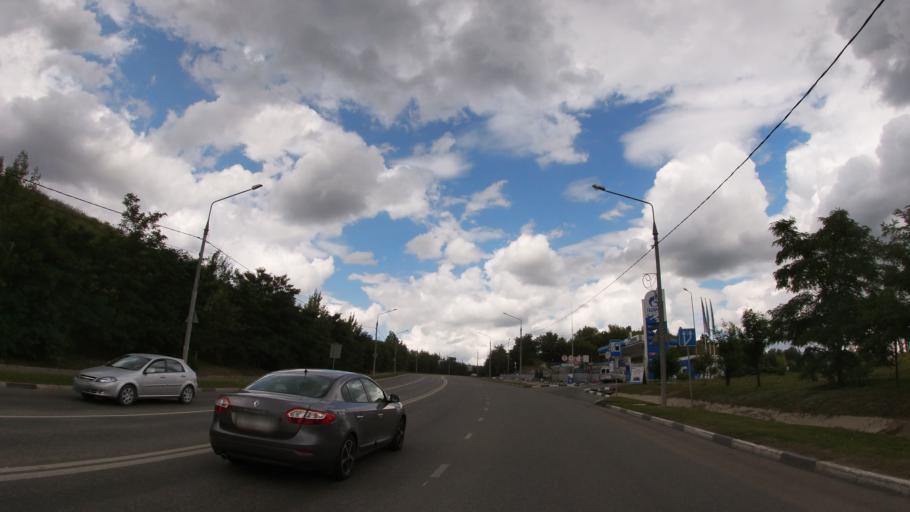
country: RU
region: Belgorod
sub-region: Belgorodskiy Rayon
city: Belgorod
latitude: 50.6095
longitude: 36.6132
